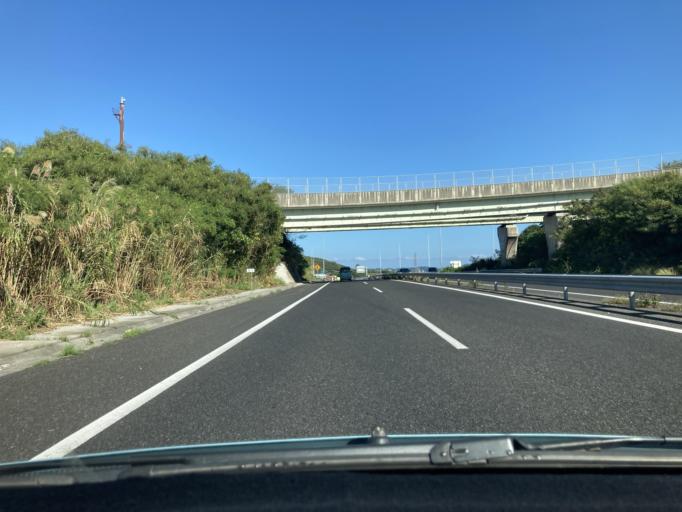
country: JP
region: Okinawa
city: Tomigusuku
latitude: 26.1724
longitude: 127.6969
